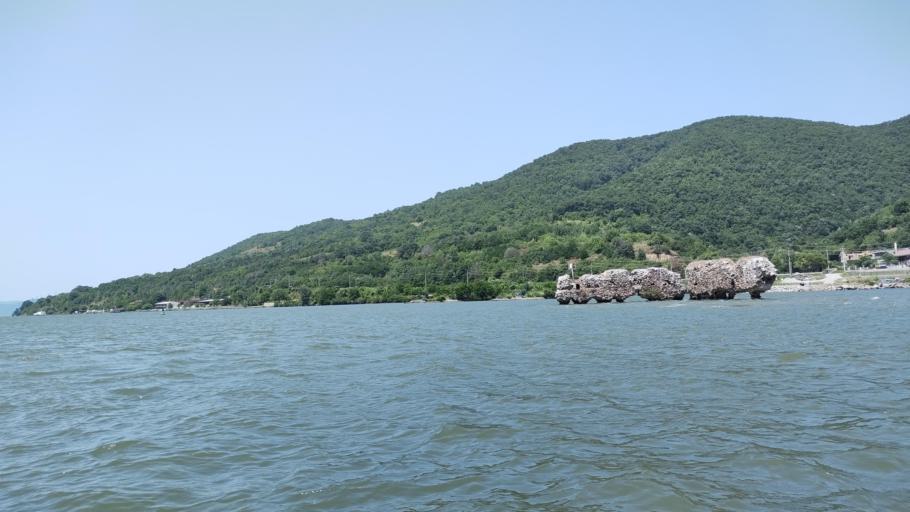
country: RO
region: Caras-Severin
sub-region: Comuna Berzasca
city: Berzasca
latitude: 44.6348
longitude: 21.9756
